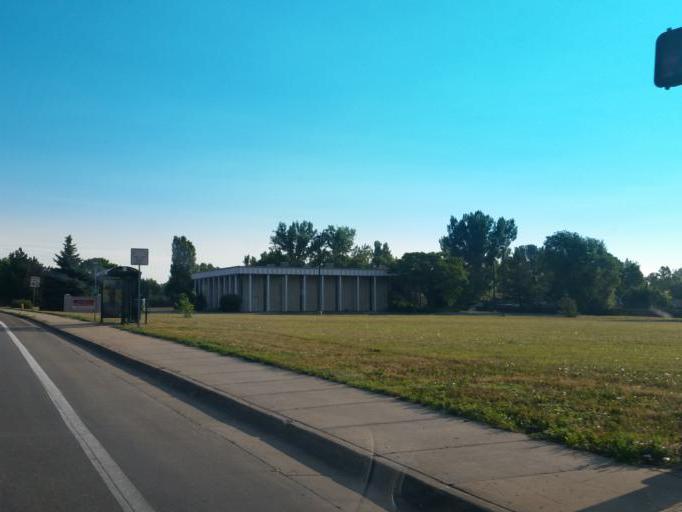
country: US
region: Colorado
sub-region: Larimer County
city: Fort Collins
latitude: 40.5531
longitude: -105.1150
